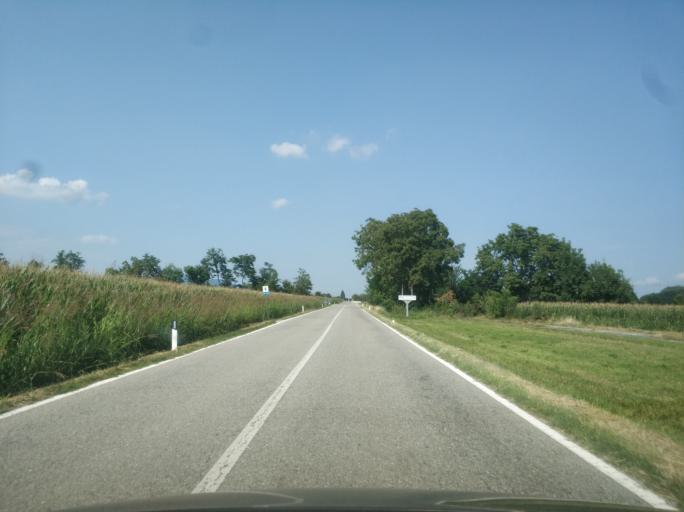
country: IT
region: Piedmont
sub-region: Provincia di Cuneo
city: Caraglio
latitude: 44.4432
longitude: 7.4536
